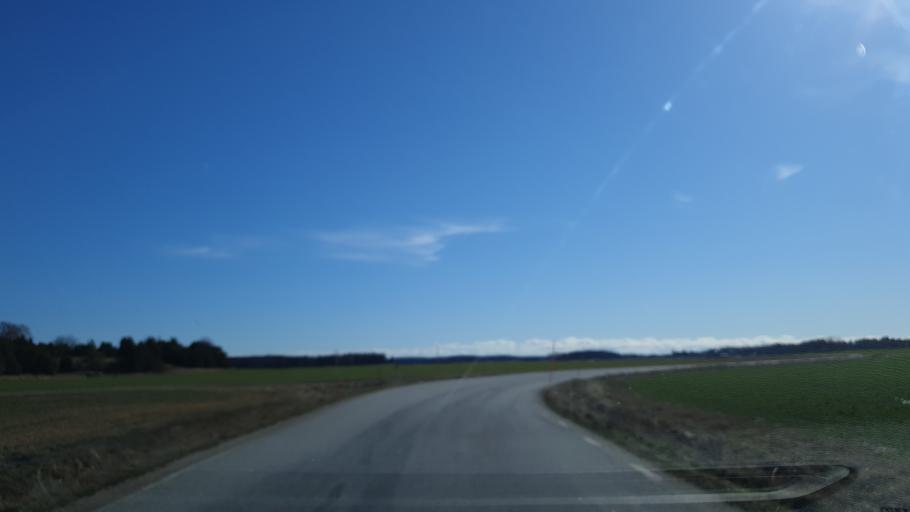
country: SE
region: Uppsala
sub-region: Enkopings Kommun
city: Grillby
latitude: 59.6023
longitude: 17.2726
